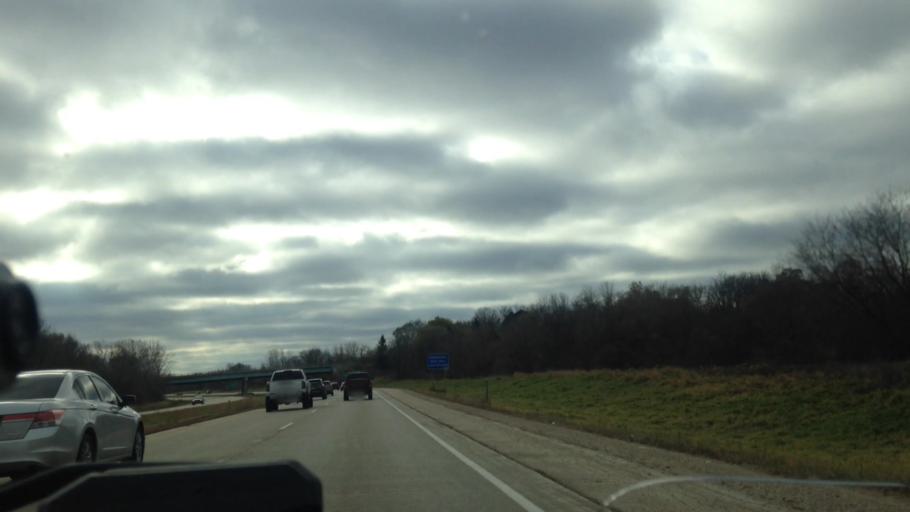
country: US
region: Wisconsin
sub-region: Washington County
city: West Bend
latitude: 43.4158
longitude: -88.2068
